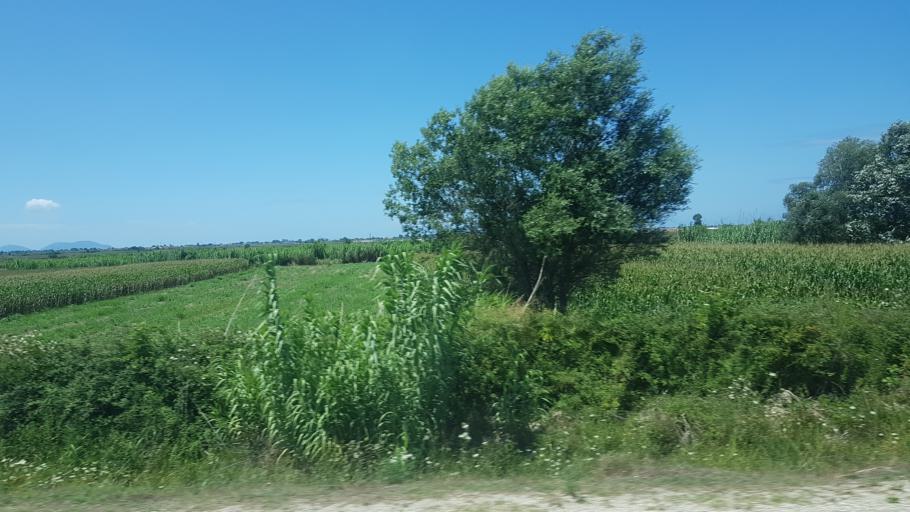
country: AL
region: Fier
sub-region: Rrethi i Fierit
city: Frakulla e Madhe
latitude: 40.6589
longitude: 19.4900
